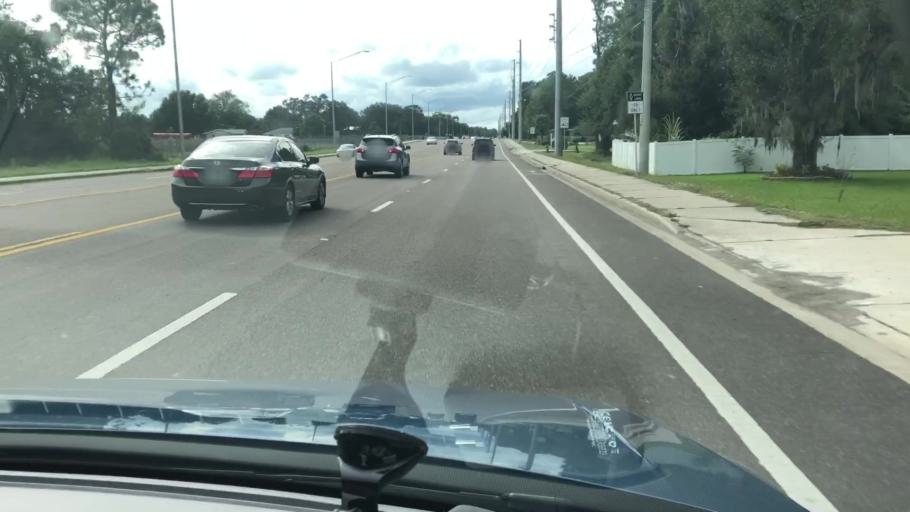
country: US
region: Florida
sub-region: Polk County
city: Gibsonia
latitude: 28.1283
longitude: -81.9607
